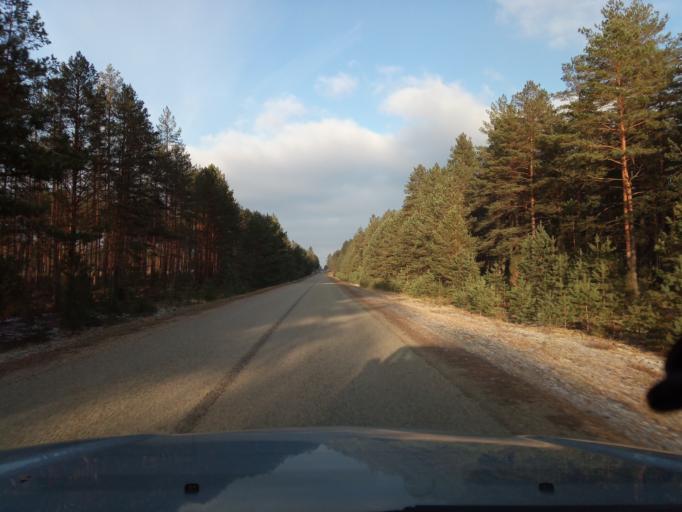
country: LT
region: Alytaus apskritis
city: Varena
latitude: 54.1696
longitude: 24.5078
